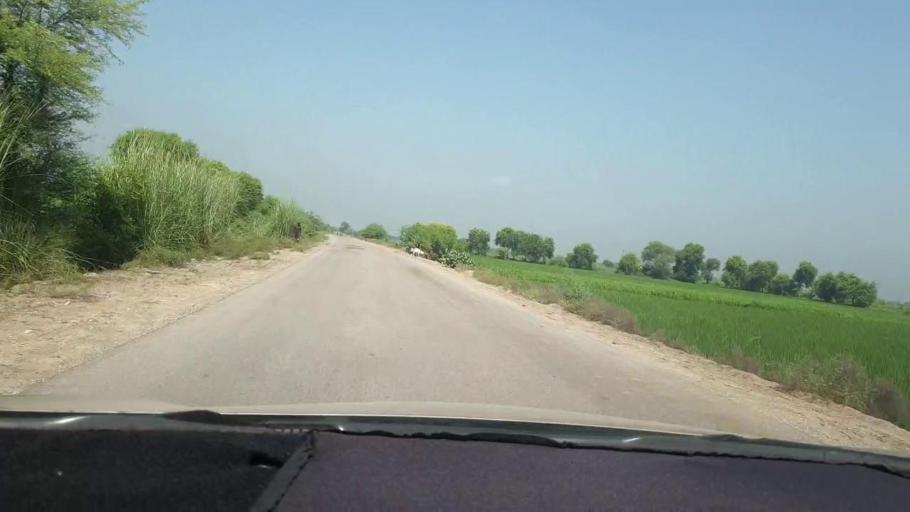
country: PK
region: Sindh
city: Miro Khan
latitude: 27.7614
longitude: 68.0772
